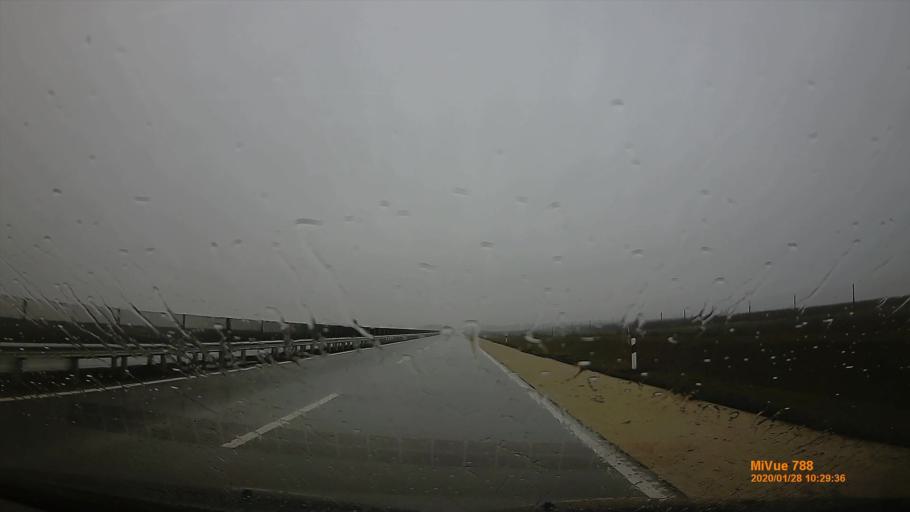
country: HU
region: Pest
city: Pilis
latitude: 47.3257
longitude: 19.5308
